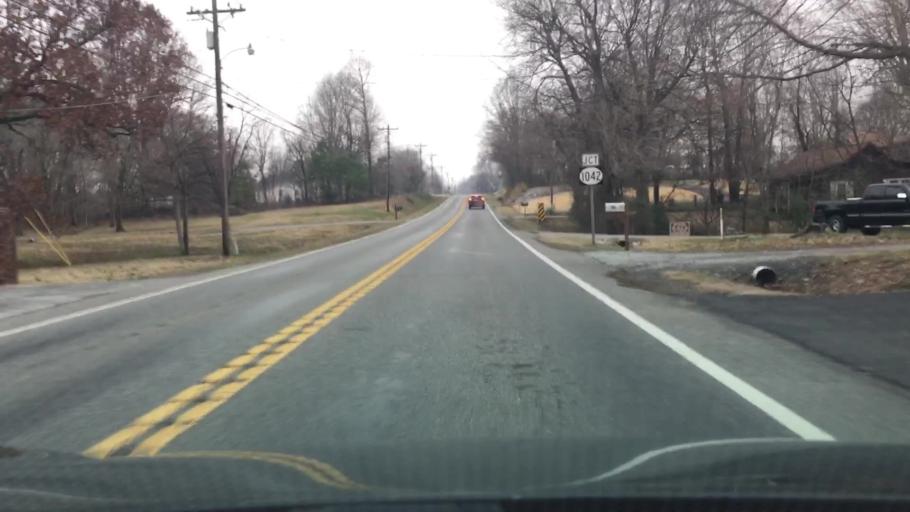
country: US
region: Kentucky
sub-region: Livingston County
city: Ledbetter
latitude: 36.9719
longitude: -88.4650
